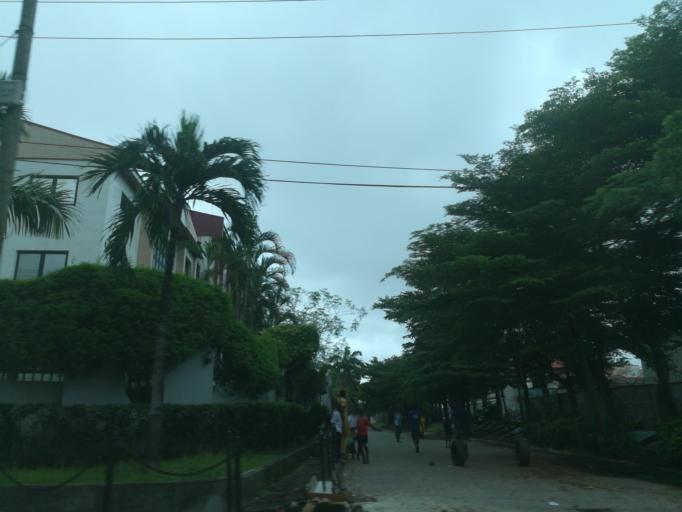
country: NG
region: Lagos
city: Ikoyi
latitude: 6.4247
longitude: 3.4221
